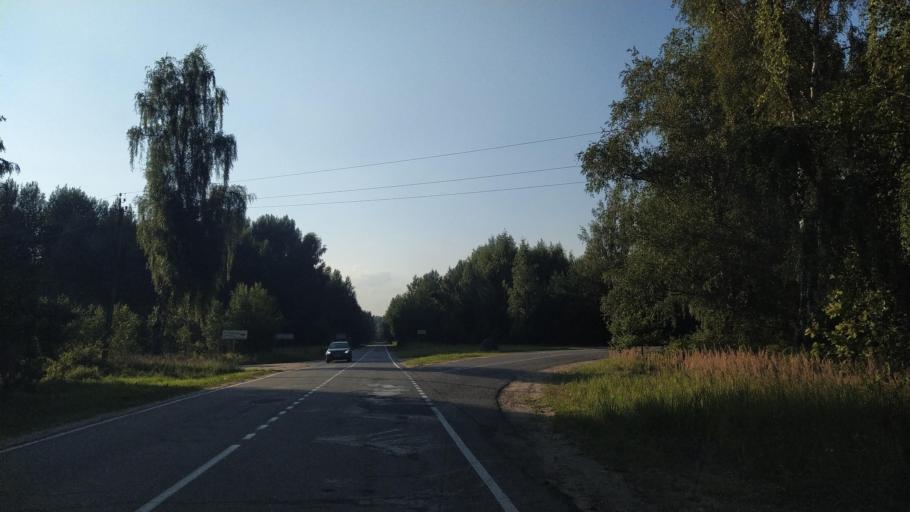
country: RU
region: Pskov
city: Pushkinskiye Gory
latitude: 57.0374
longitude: 28.9119
